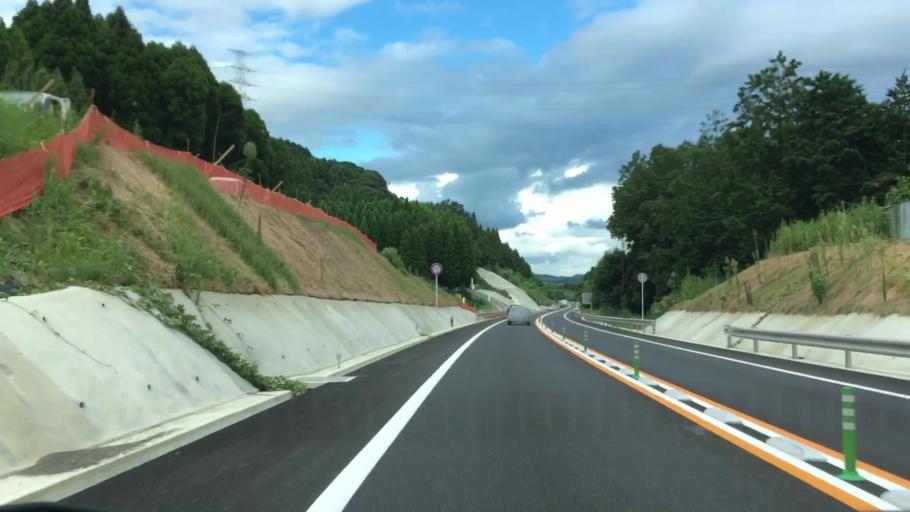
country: JP
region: Saga Prefecture
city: Imaricho-ko
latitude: 33.3143
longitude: 129.9190
